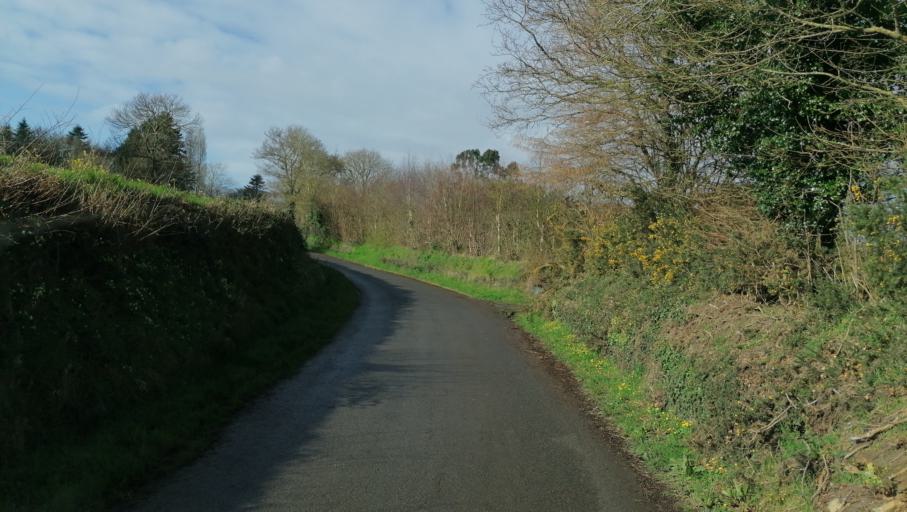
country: FR
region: Brittany
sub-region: Departement des Cotes-d'Armor
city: Plouha
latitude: 48.6570
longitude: -2.9165
